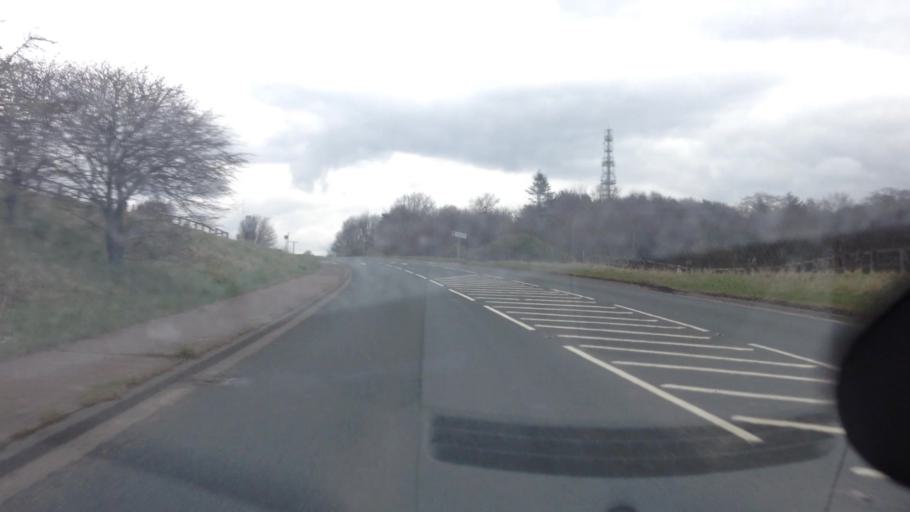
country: GB
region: England
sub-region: Calderdale
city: Elland
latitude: 53.6723
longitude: -1.8196
